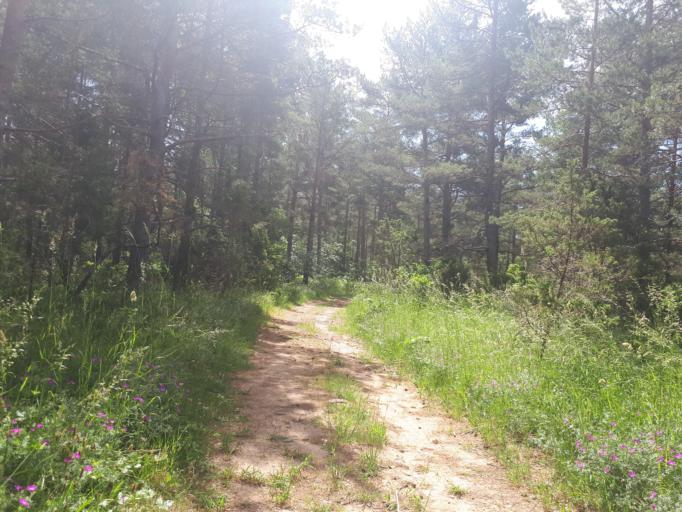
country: SE
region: Gotland
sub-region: Gotland
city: Visby
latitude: 57.6063
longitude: 18.2908
